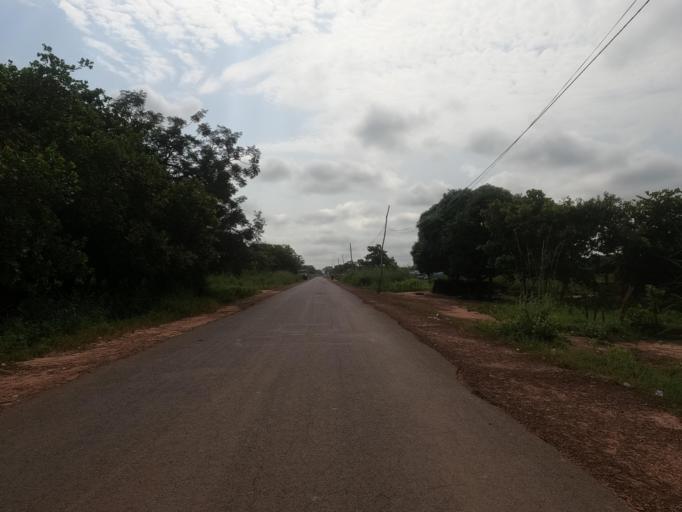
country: SN
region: Ziguinchor
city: Adeane
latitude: 12.3990
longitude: -15.7901
